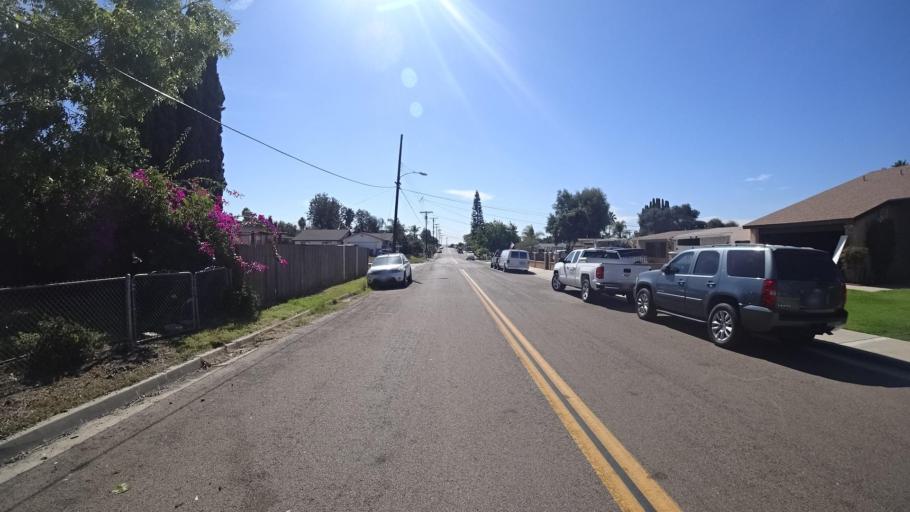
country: US
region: California
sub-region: San Diego County
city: La Presa
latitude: 32.7041
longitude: -117.0041
